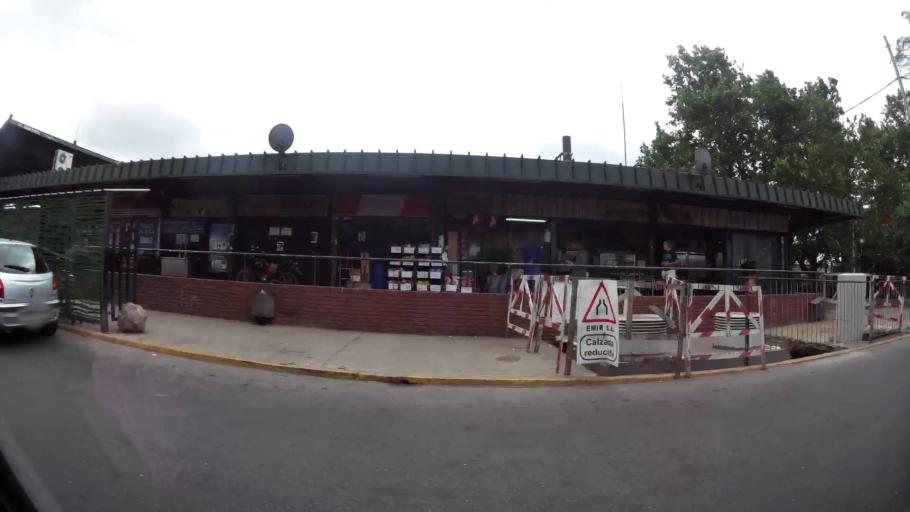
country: AR
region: Buenos Aires
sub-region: Partido de Ezeiza
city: Ezeiza
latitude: -34.8552
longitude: -58.5238
